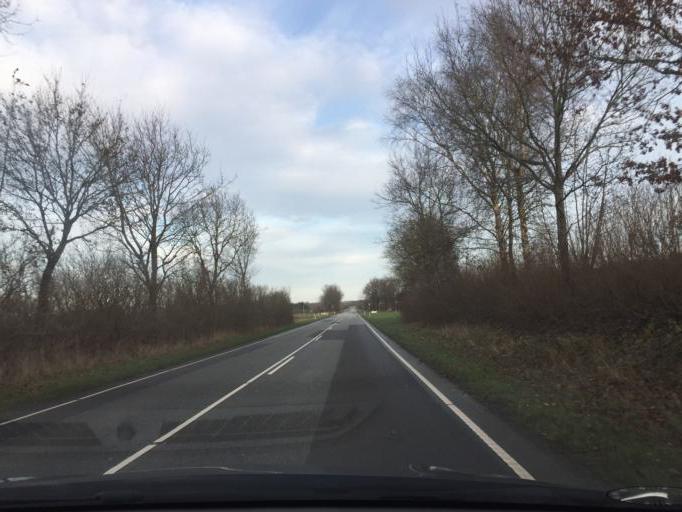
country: DK
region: South Denmark
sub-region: Faaborg-Midtfyn Kommune
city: Ringe
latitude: 55.2121
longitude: 10.4236
